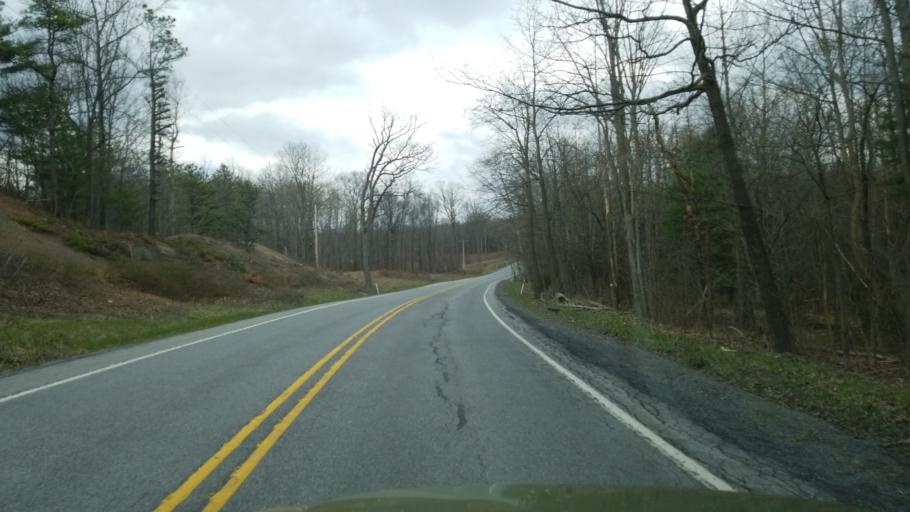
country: US
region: Pennsylvania
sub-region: Blair County
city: Tipton
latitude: 40.7457
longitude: -78.3914
